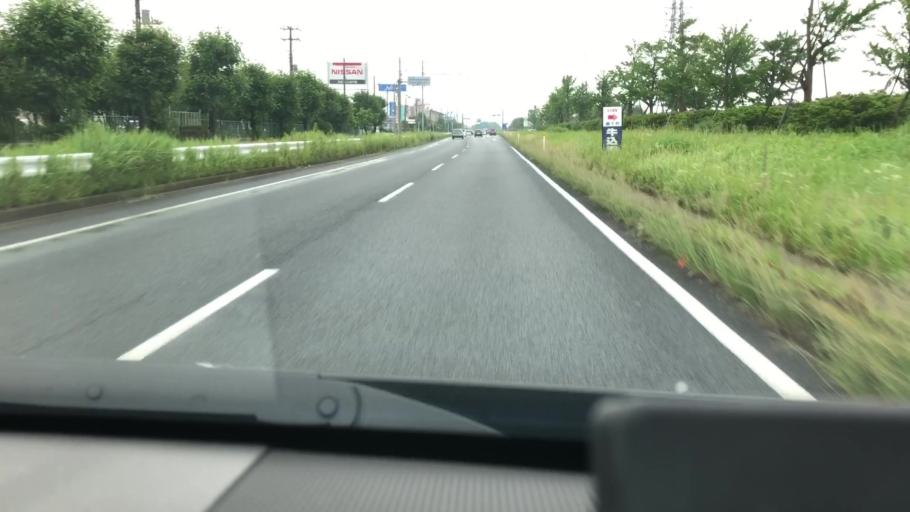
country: JP
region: Chiba
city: Kisarazu
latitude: 35.4458
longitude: 139.9795
